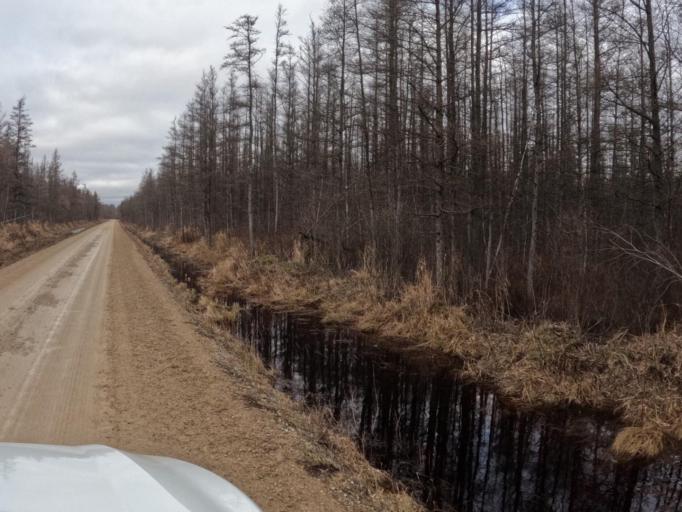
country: CA
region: Ontario
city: Shelburne
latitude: 43.9004
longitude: -80.4087
